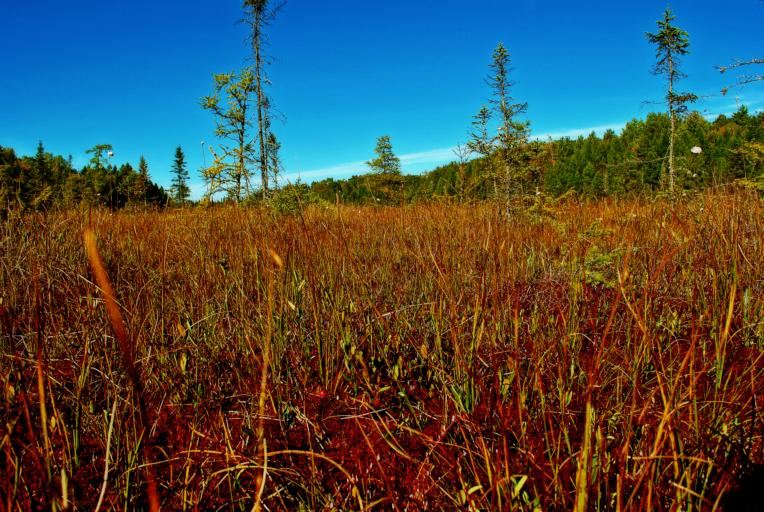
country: US
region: Wisconsin
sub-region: Sawyer County
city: Hayward
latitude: 46.0134
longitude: -91.5333
